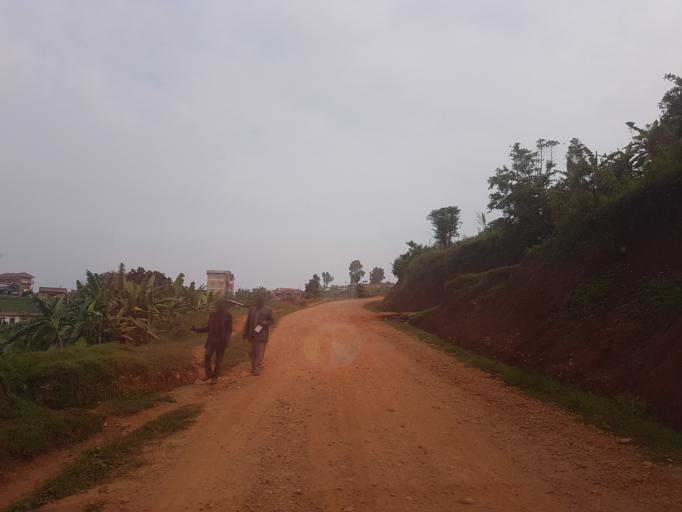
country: UG
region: Western Region
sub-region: Kanungu District
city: Kanungu
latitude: -0.8964
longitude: 29.7781
